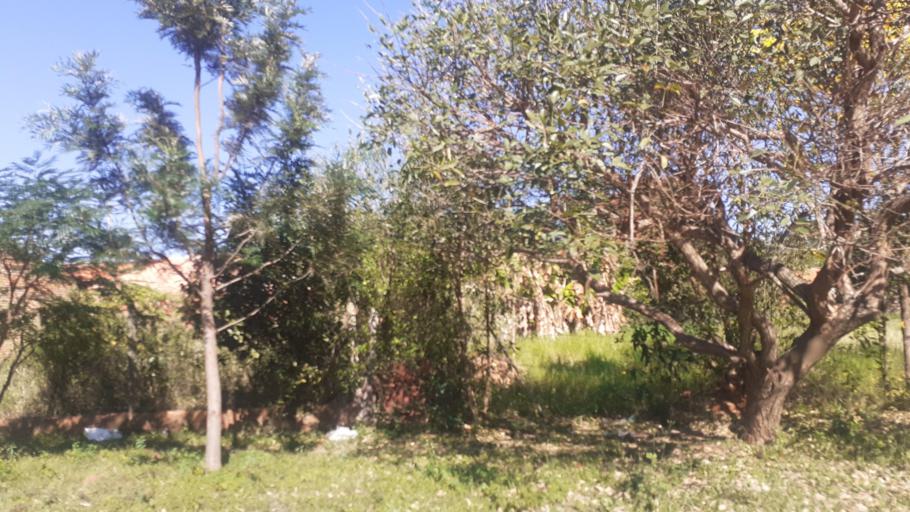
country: PY
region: Misiones
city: San Juan Bautista
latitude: -26.6650
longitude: -57.1260
